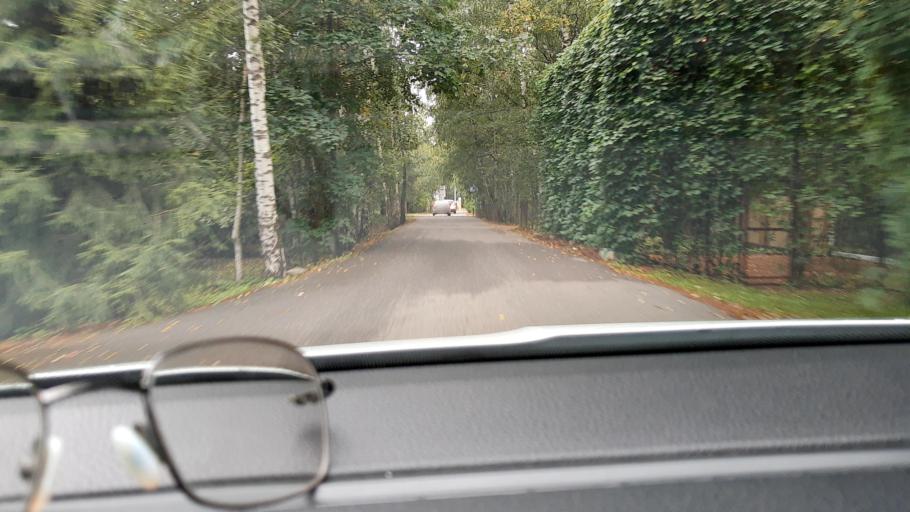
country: RU
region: Moskovskaya
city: Kokoshkino
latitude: 55.5927
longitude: 37.1701
